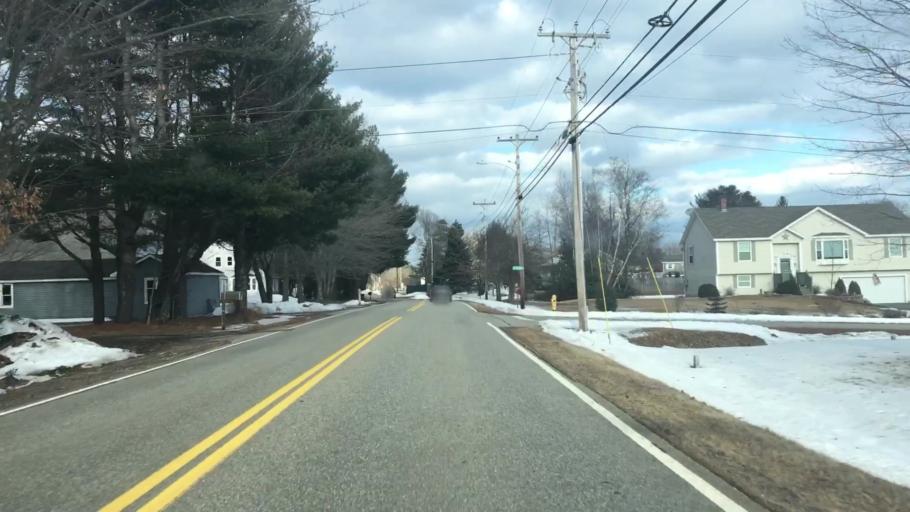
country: US
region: Maine
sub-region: York County
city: Biddeford
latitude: 43.4540
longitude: -70.4312
